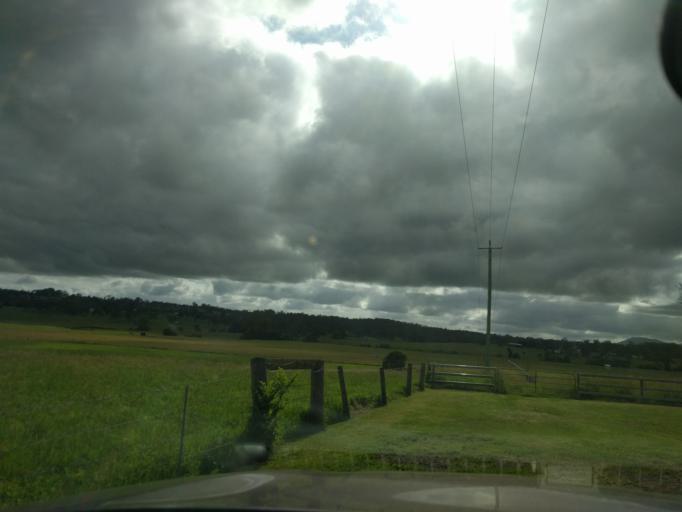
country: AU
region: Queensland
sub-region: Logan
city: Cedar Vale
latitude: -28.0087
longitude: 152.9980
